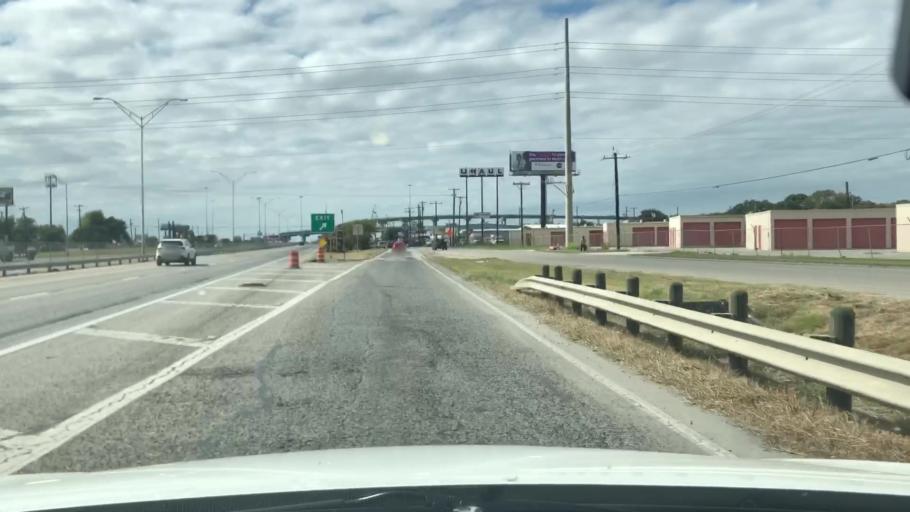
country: US
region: Texas
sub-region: Bexar County
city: Lackland Air Force Base
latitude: 29.3994
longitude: -98.6422
